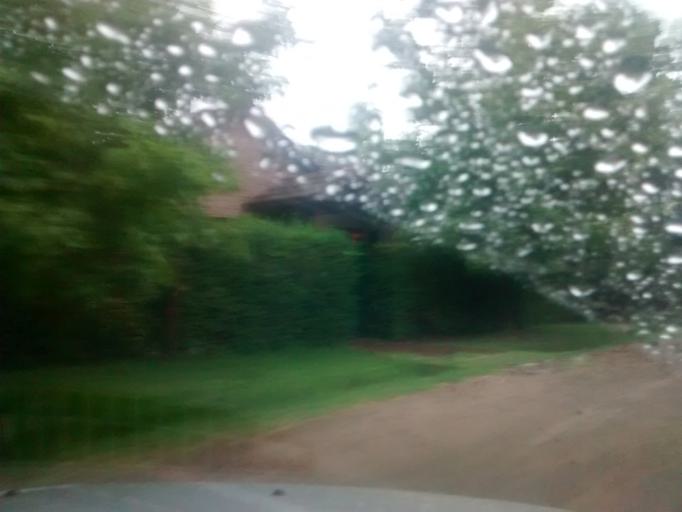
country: AR
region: Buenos Aires
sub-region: Partido de La Plata
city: La Plata
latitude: -34.8825
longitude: -58.0658
